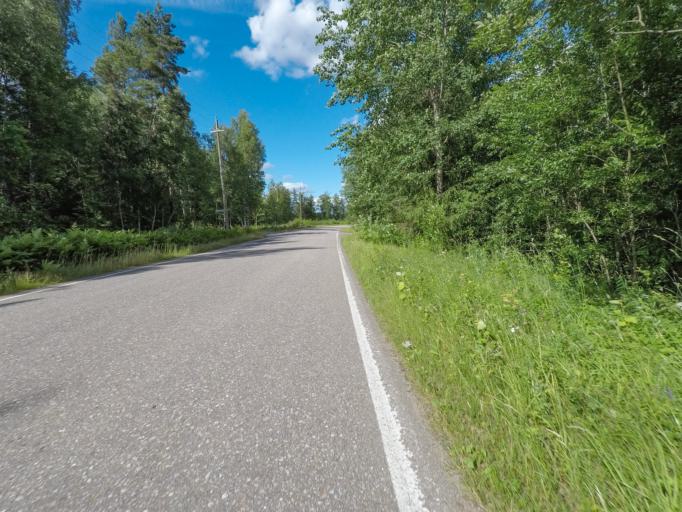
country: FI
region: South Karelia
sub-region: Lappeenranta
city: Joutseno
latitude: 61.1147
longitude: 28.3727
